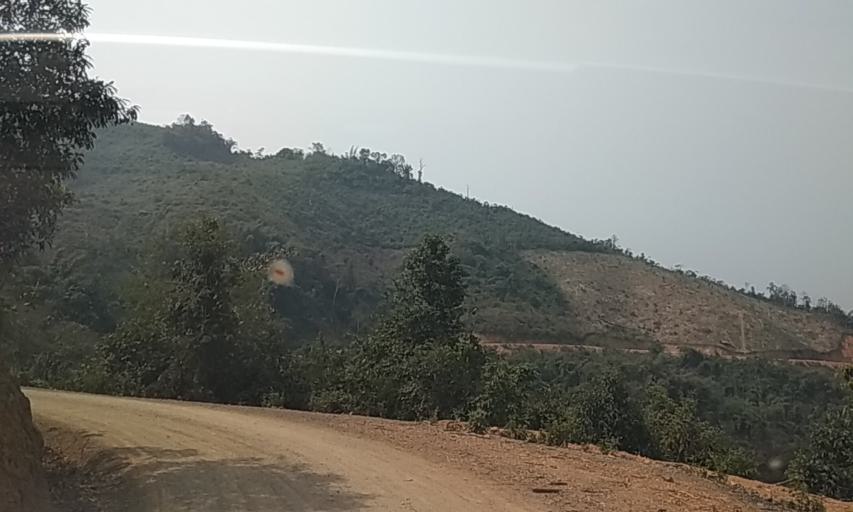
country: LA
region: Phongsali
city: Phongsali
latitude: 21.4780
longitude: 102.4404
